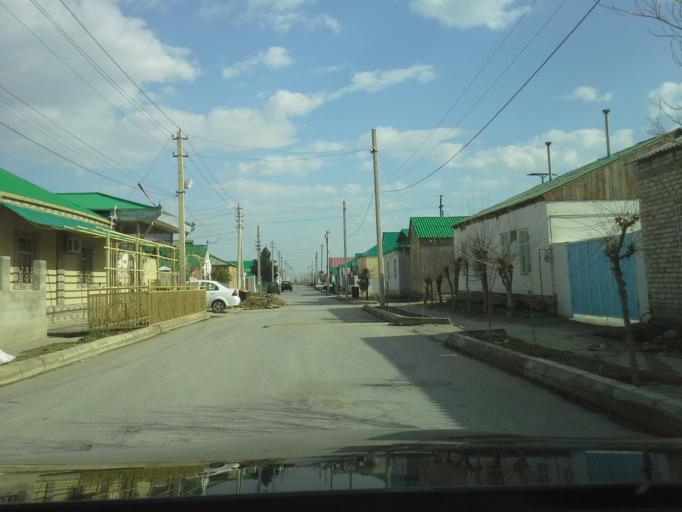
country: TM
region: Ahal
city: Ashgabat
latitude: 37.9919
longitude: 58.2935
